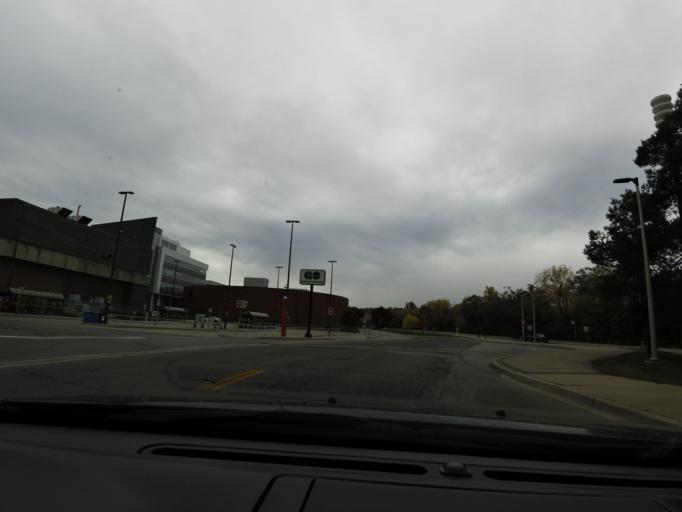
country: CA
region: Ontario
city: Hamilton
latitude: 43.2623
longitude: -79.9230
